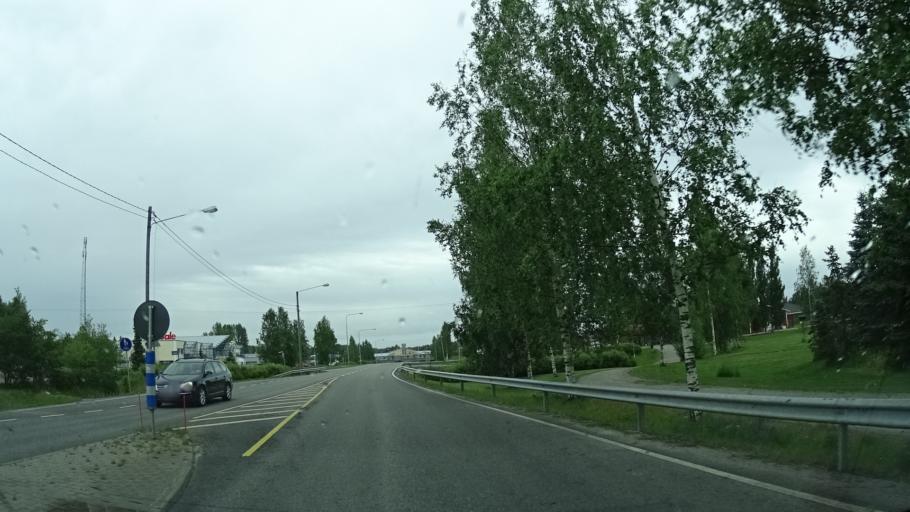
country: FI
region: Varsinais-Suomi
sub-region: Loimaa
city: Aura
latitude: 60.6500
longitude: 22.5860
